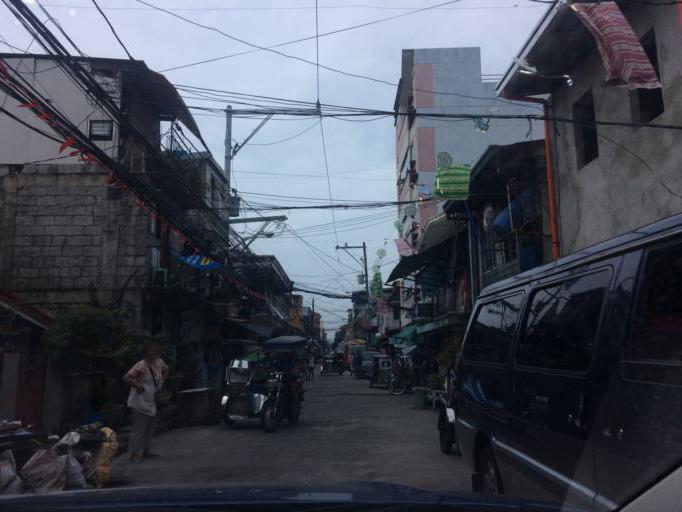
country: PH
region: Metro Manila
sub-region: Makati City
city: Makati City
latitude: 14.5408
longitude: 121.0030
